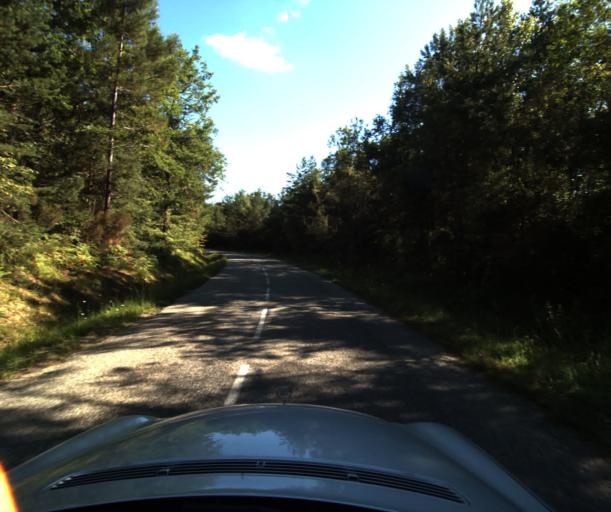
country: FR
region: Languedoc-Roussillon
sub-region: Departement de l'Aude
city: Chalabre
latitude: 42.9651
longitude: 1.9889
